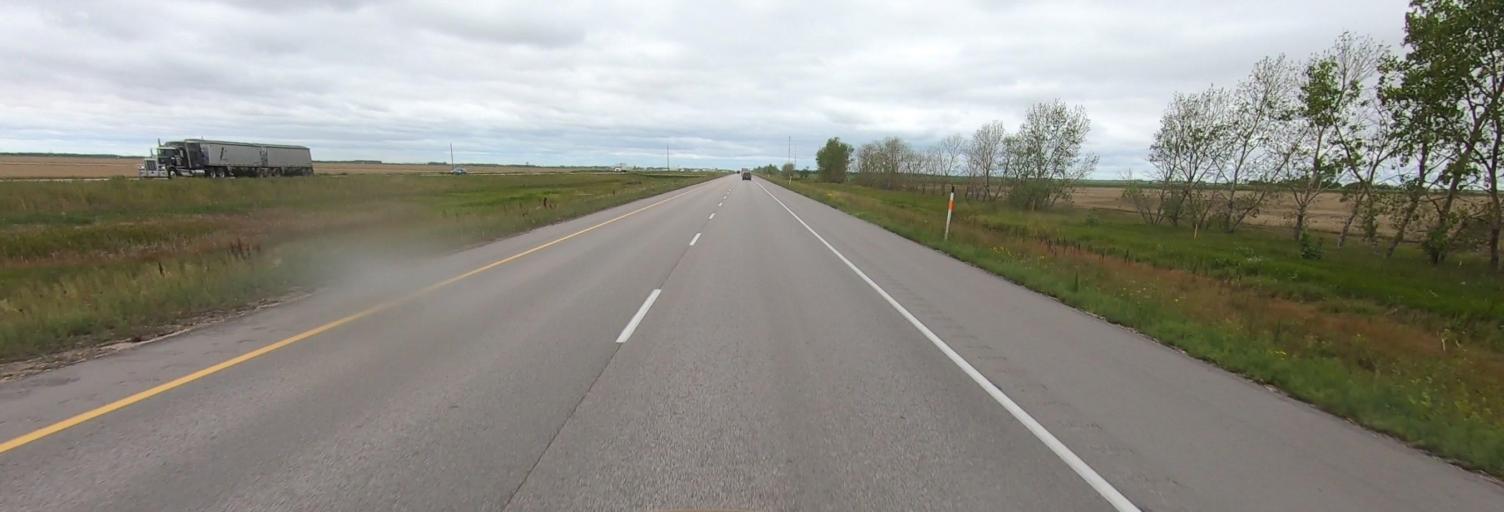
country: CA
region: Manitoba
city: Headingley
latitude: 49.8933
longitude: -97.6840
